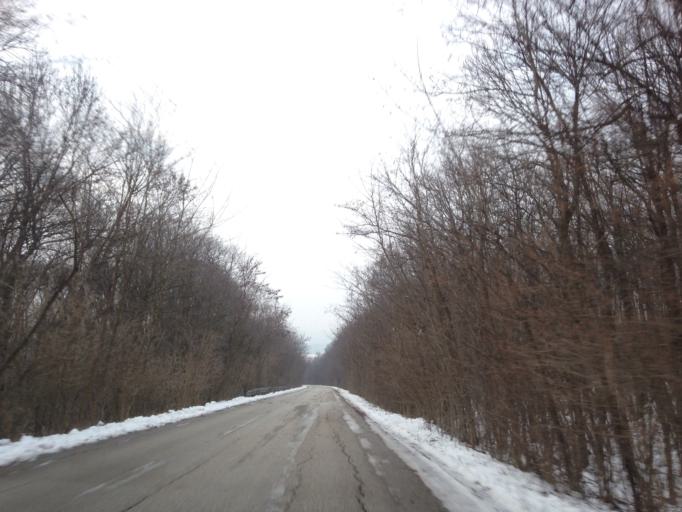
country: SK
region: Nitriansky
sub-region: Okres Nitra
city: Vrable
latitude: 48.0971
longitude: 18.3633
